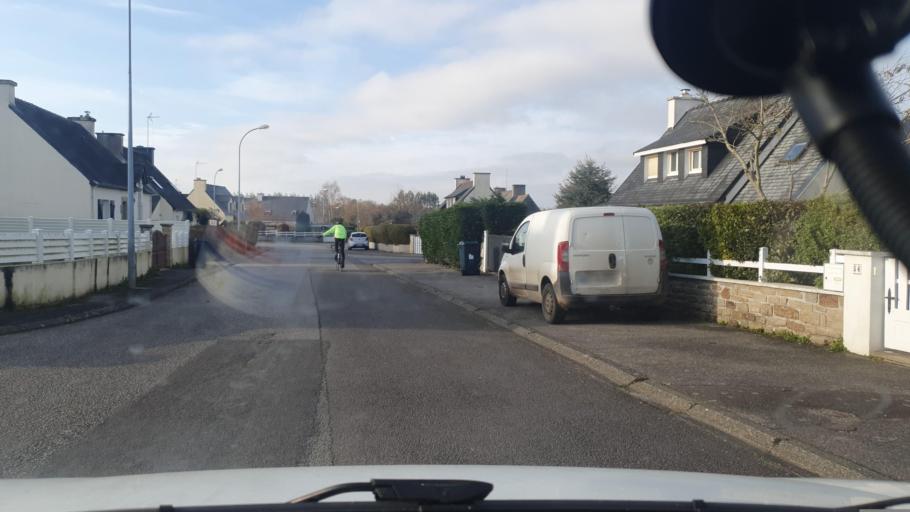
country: FR
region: Brittany
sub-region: Departement du Finistere
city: Briec
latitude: 48.1040
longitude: -4.0068
